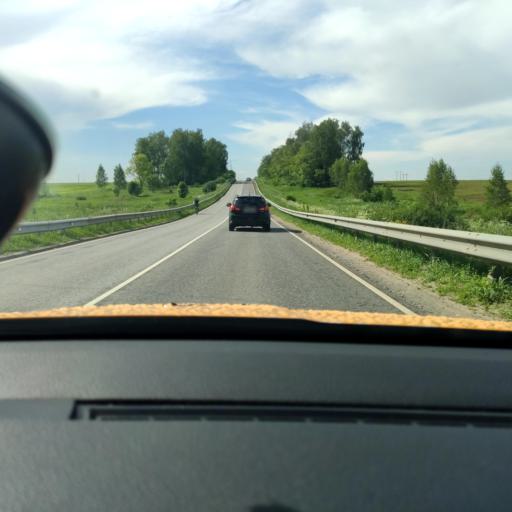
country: RU
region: Moskovskaya
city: Stupino
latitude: 54.9385
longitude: 38.0387
